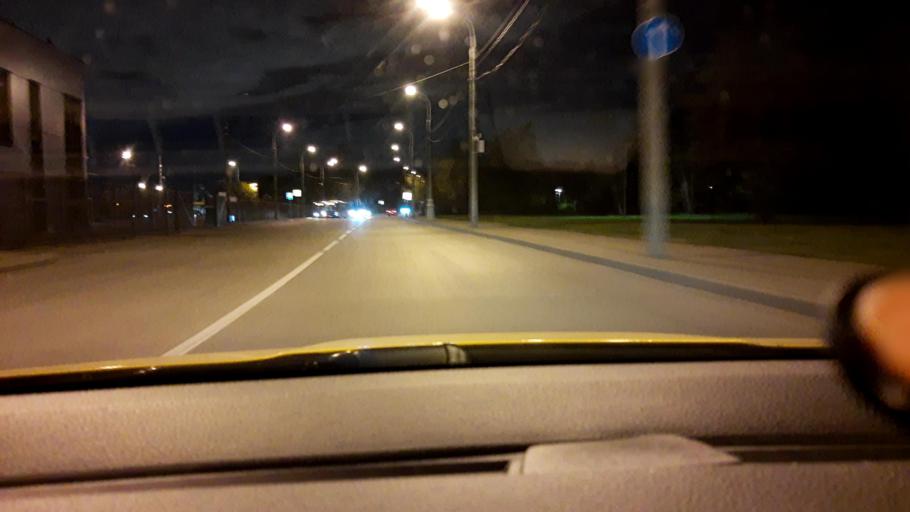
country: RU
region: Moscow
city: Kuz'minki
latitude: 55.6750
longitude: 37.7981
